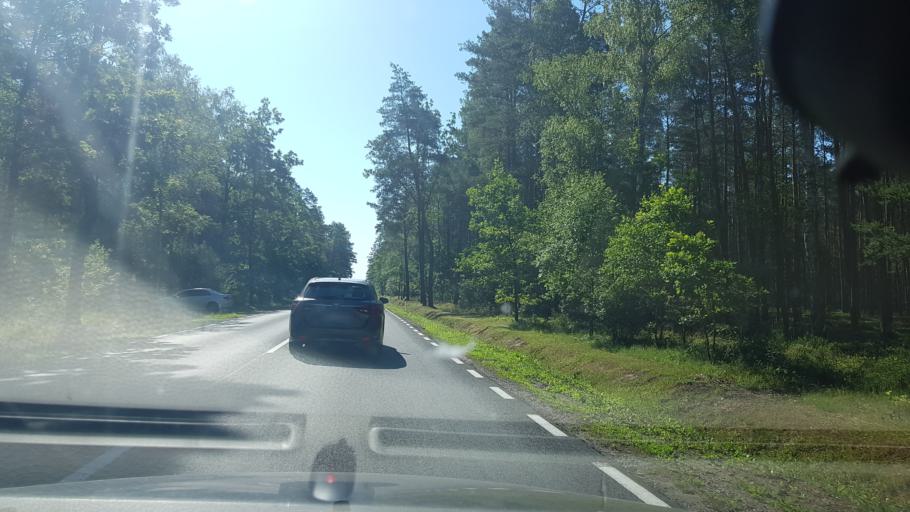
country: PL
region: Masovian Voivodeship
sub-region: Powiat wyszkowski
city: Branszczyk
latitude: 52.5666
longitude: 21.5534
